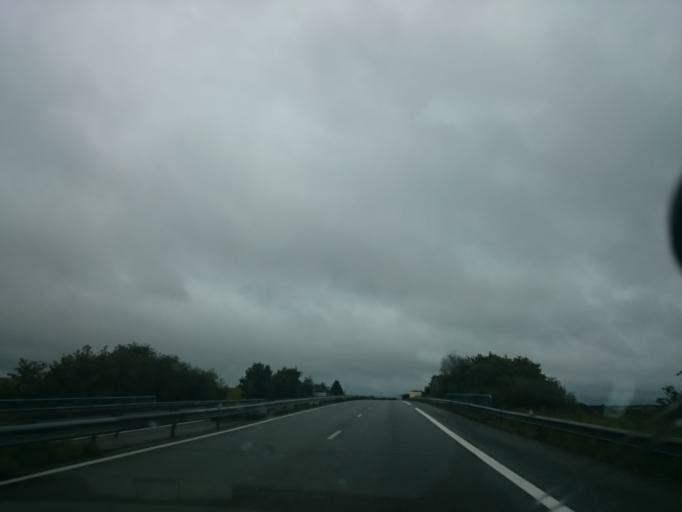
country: FR
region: Brittany
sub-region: Departement du Finistere
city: Chateaulin
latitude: 48.2306
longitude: -4.0956
